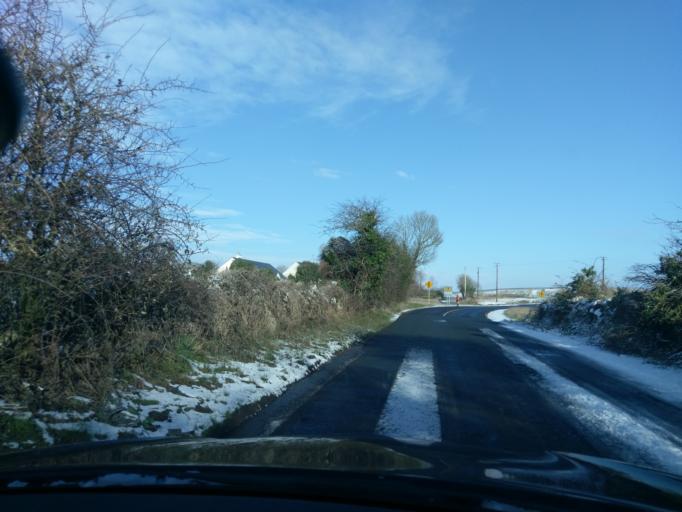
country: IE
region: Connaught
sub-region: County Galway
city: Oranmore
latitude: 53.1971
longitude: -8.8329
